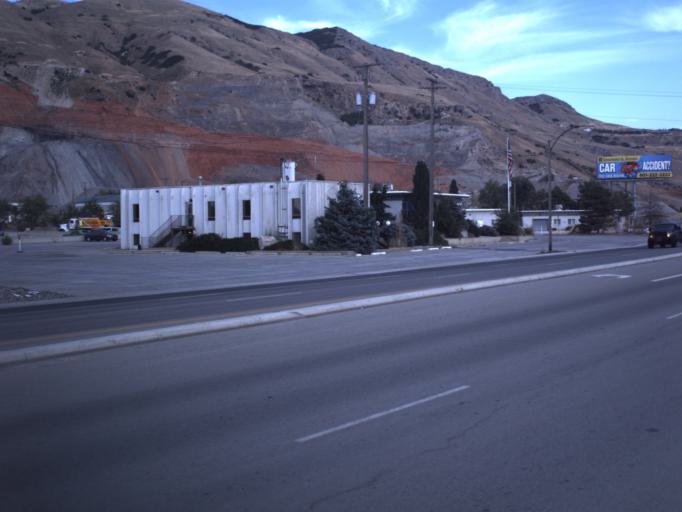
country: US
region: Utah
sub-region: Davis County
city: North Salt Lake
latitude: 40.8053
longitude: -111.9173
